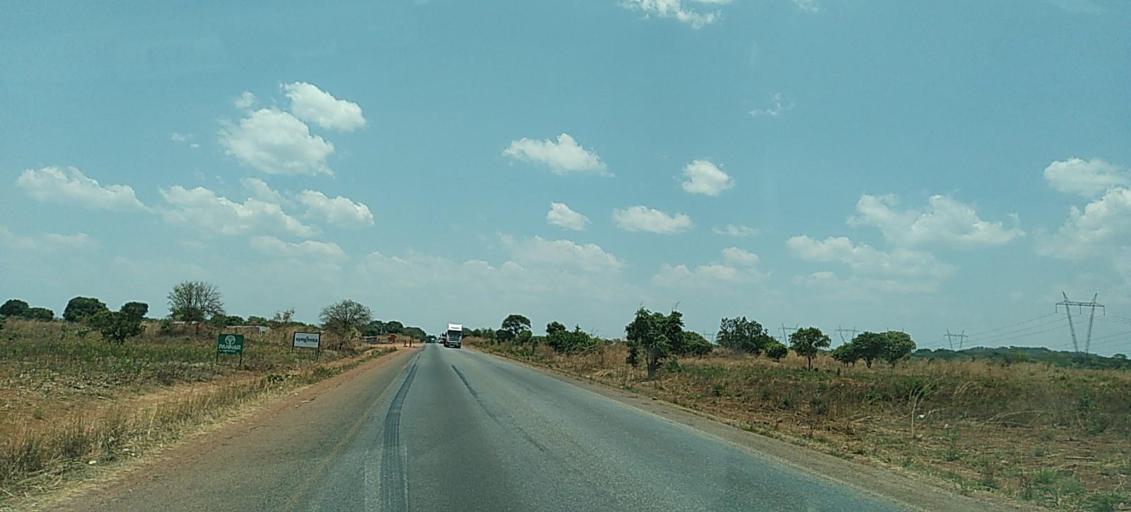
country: ZM
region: Central
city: Kapiri Mposhi
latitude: -13.7057
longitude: 28.6302
